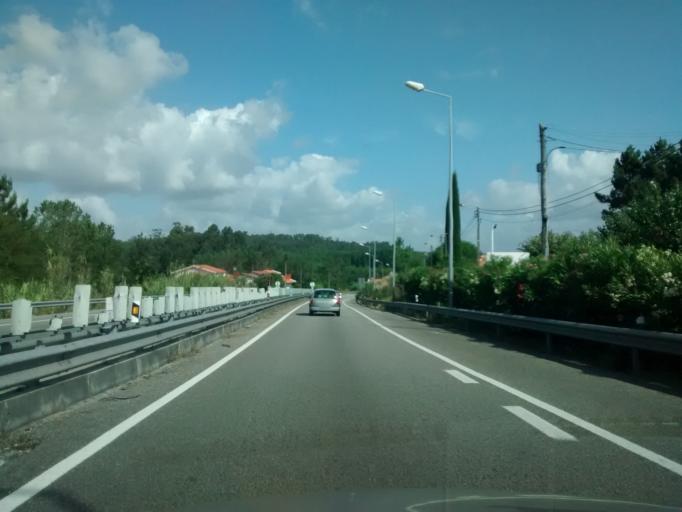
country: PT
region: Aveiro
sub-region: Oliveira do Bairro
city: Oliveira do Bairro
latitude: 40.5254
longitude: -8.5069
